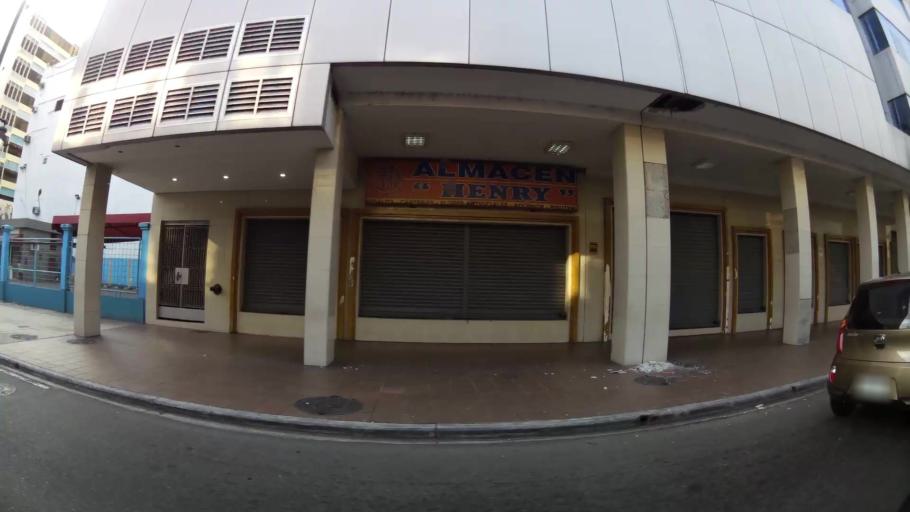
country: EC
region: Guayas
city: Guayaquil
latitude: -2.1935
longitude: -79.8847
